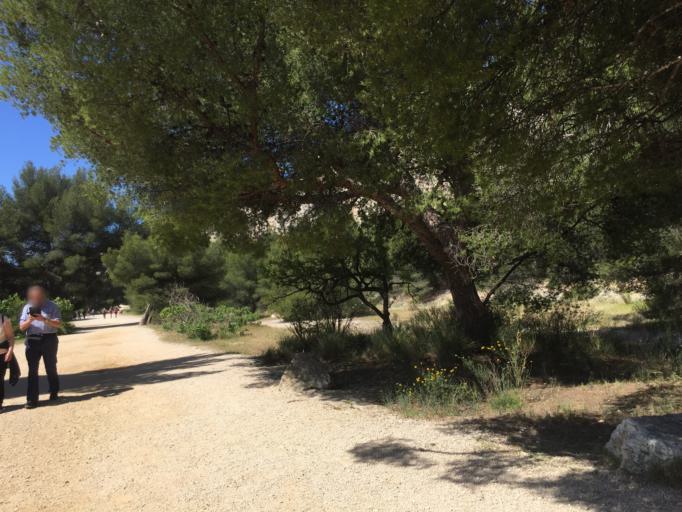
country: FR
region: Provence-Alpes-Cote d'Azur
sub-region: Departement des Bouches-du-Rhone
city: Cassis
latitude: 43.2089
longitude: 5.5175
